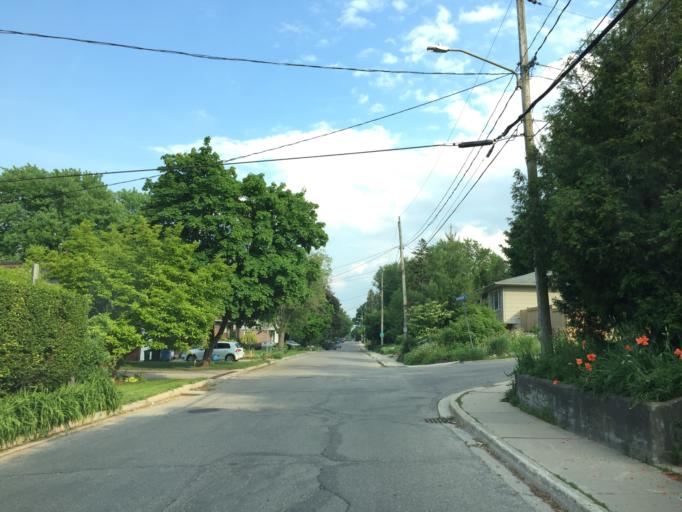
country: CA
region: Ontario
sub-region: Wellington County
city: Guelph
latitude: 43.5539
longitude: -80.2703
